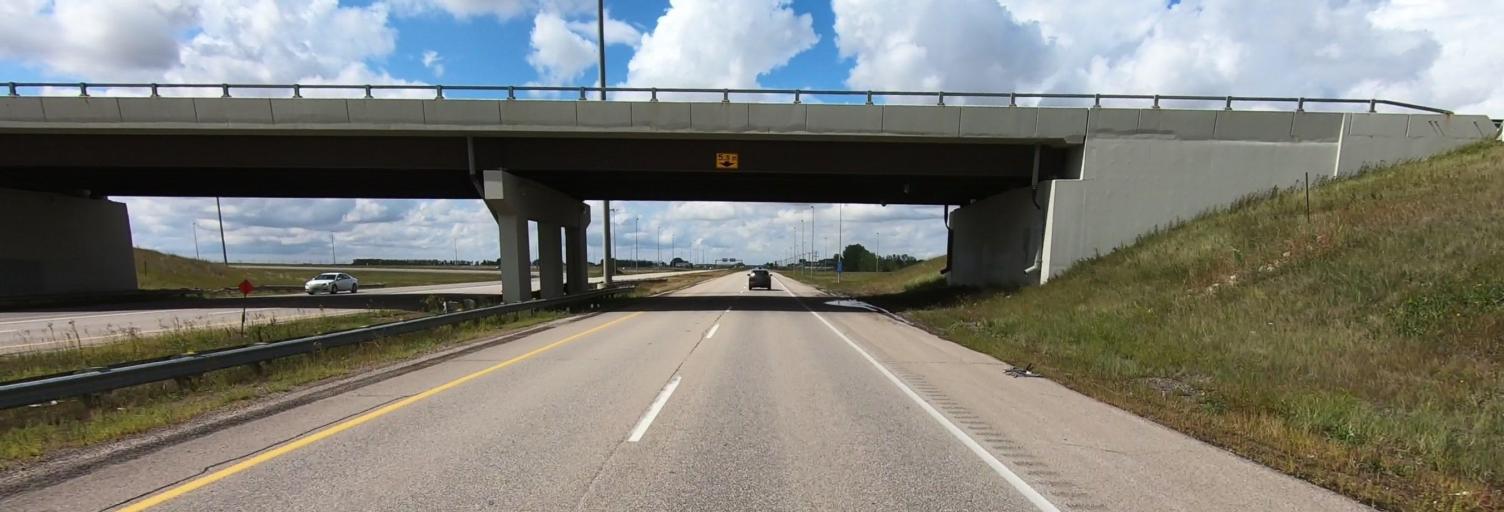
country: CA
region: Saskatchewan
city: Regina
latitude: 50.3969
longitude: -104.6433
